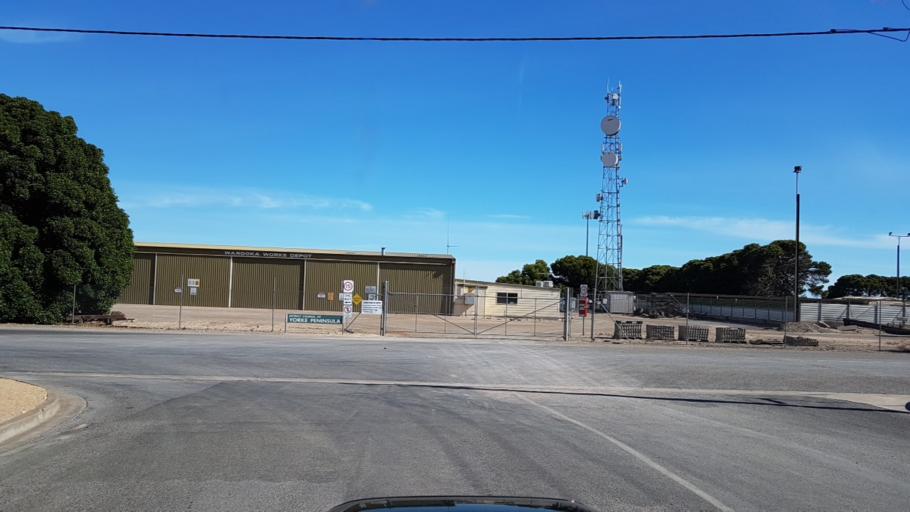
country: AU
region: South Australia
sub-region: Yorke Peninsula
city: Honiton
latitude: -34.9922
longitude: 137.3998
